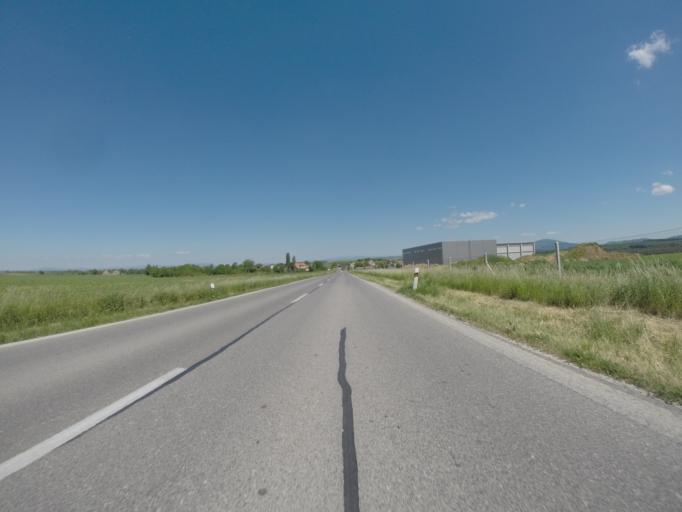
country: SK
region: Nitriansky
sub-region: Okres Nitra
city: Nitra
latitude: 48.5233
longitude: 18.0478
